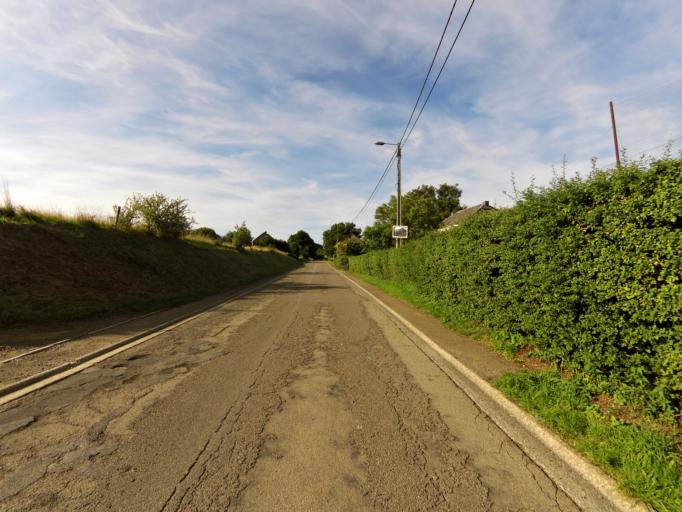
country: BE
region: Wallonia
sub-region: Province du Luxembourg
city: Erezee
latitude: 50.2640
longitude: 5.5570
